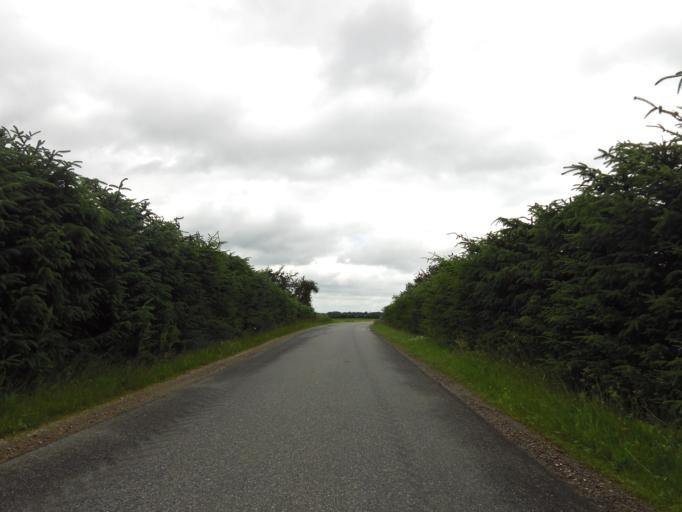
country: DK
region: South Denmark
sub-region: Kolding Kommune
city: Vamdrup
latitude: 55.3441
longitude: 9.1983
